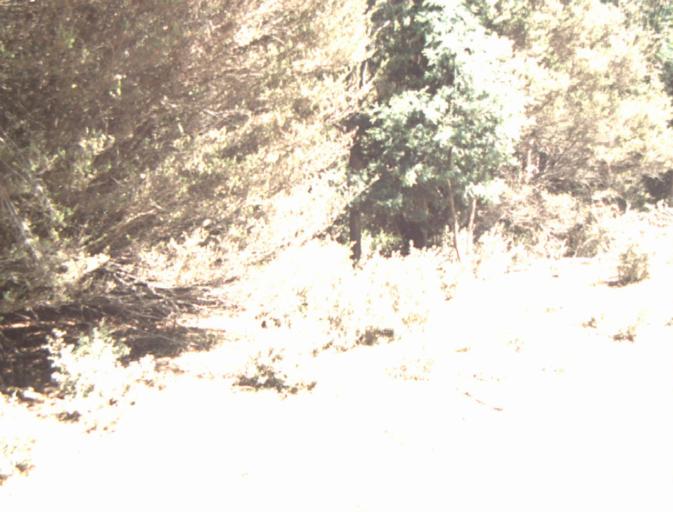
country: AU
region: Tasmania
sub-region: Dorset
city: Scottsdale
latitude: -41.3588
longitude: 147.4270
